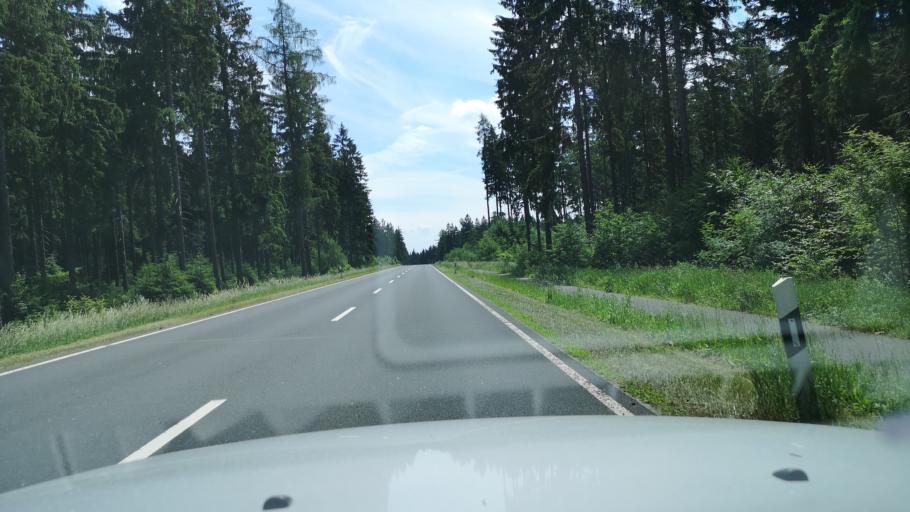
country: DE
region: Bavaria
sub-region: Upper Franconia
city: Ludwigsstadt
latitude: 50.4485
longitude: 11.3586
